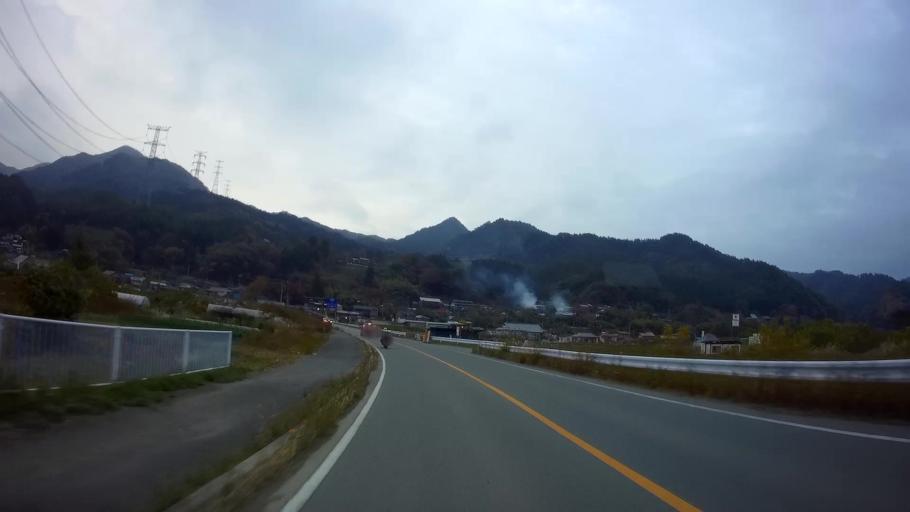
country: JP
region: Gunma
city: Nakanojomachi
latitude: 36.5610
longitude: 138.7580
